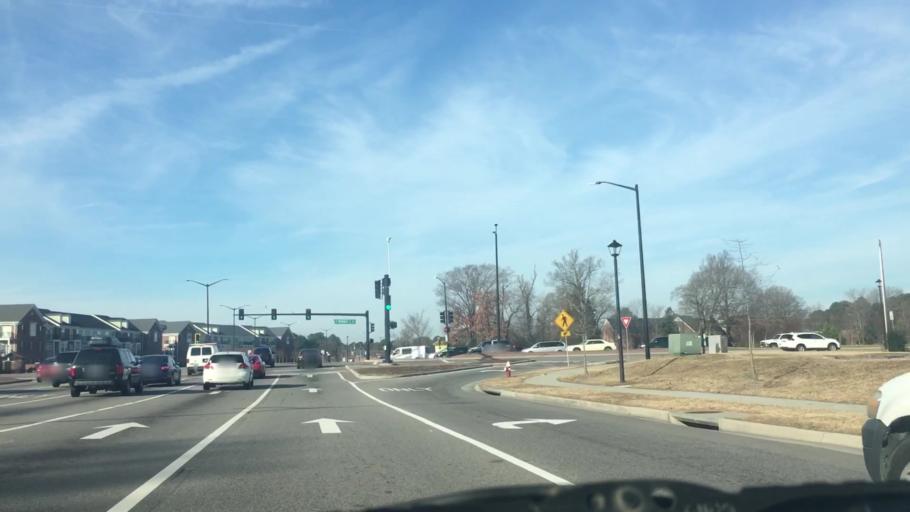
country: US
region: Virginia
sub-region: City of Chesapeake
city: Chesapeake
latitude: 36.8254
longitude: -76.1599
